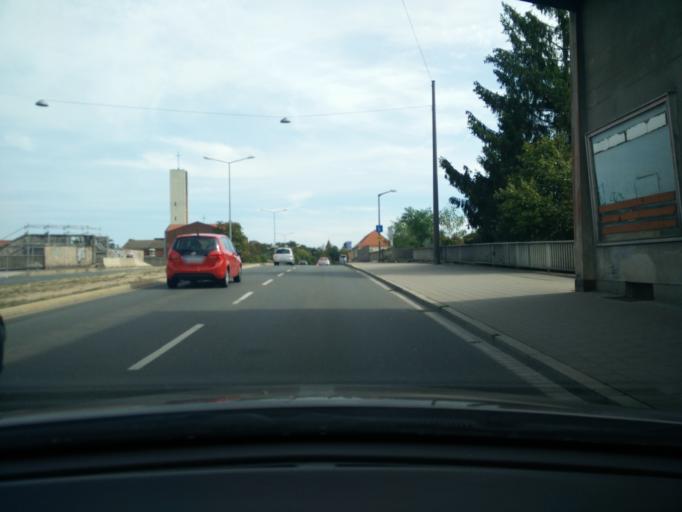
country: DE
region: Bavaria
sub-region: Regierungsbezirk Mittelfranken
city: Furth
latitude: 49.4826
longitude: 10.9664
